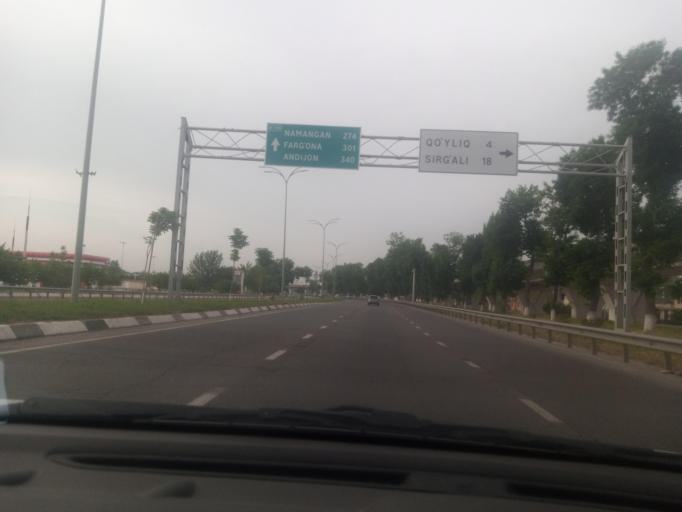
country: UZ
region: Toshkent Shahri
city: Bektemir
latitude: 41.2739
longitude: 69.3620
